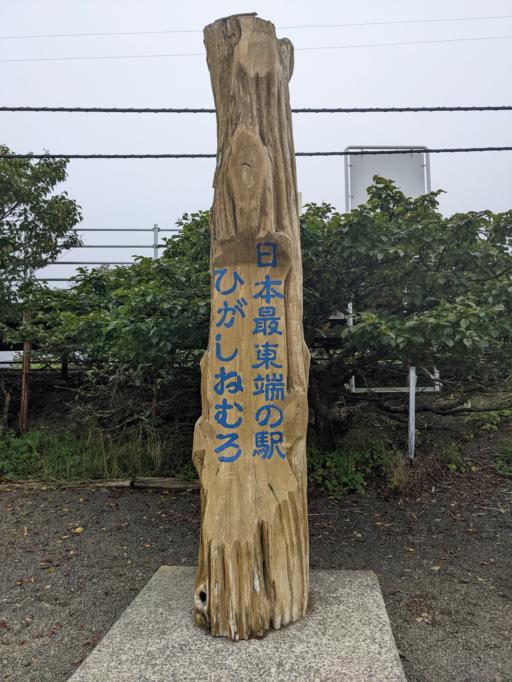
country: JP
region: Hokkaido
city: Nemuro
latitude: 43.3236
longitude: 145.5974
